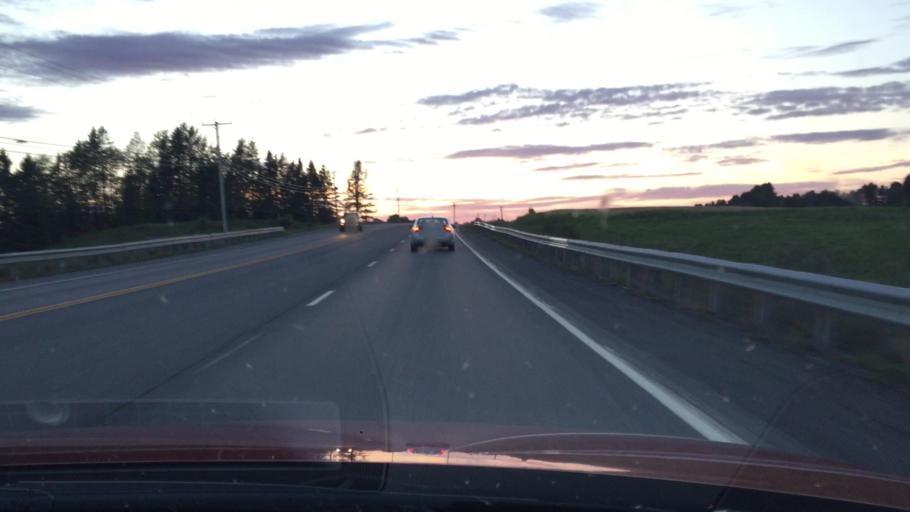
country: US
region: Maine
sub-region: Aroostook County
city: Easton
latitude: 46.5428
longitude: -67.9167
